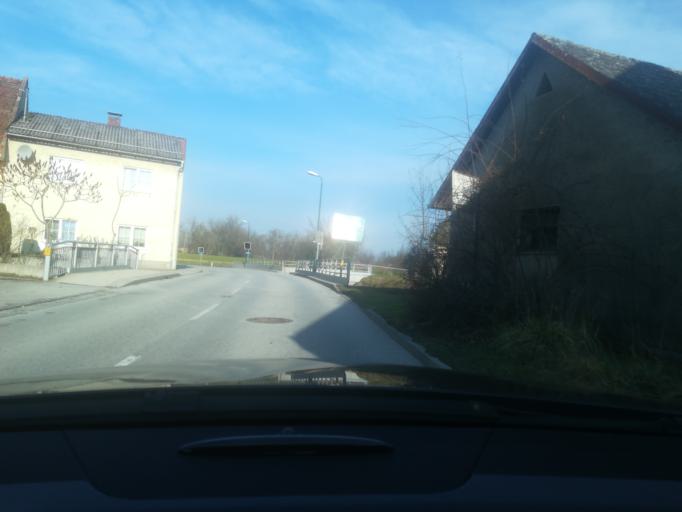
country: AT
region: Upper Austria
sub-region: Wels-Land
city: Buchkirchen
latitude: 48.2861
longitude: 14.0309
